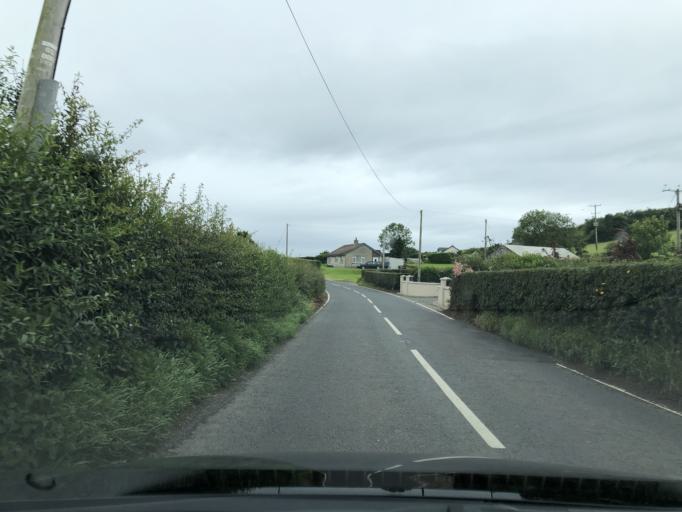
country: GB
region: Northern Ireland
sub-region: Down District
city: Dundrum
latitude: 54.2620
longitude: -5.7828
